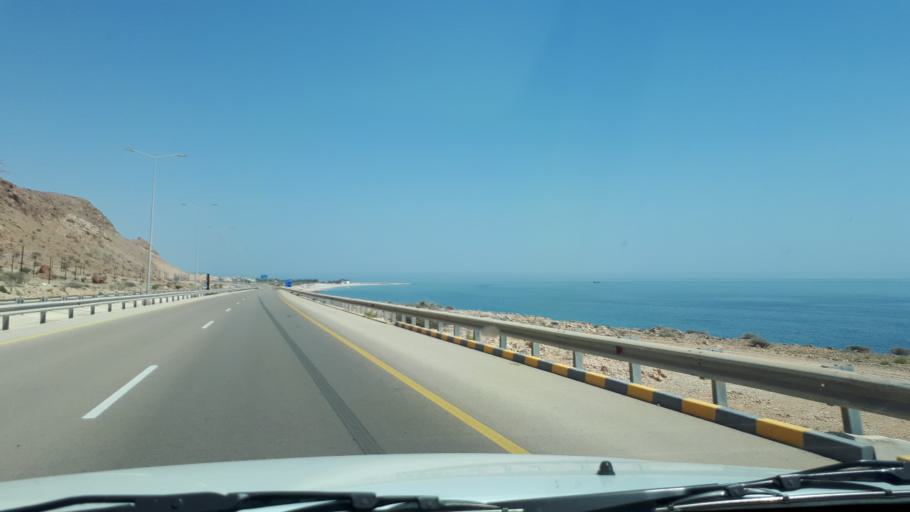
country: OM
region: Ash Sharqiyah
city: Sur
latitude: 22.8074
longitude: 59.2673
